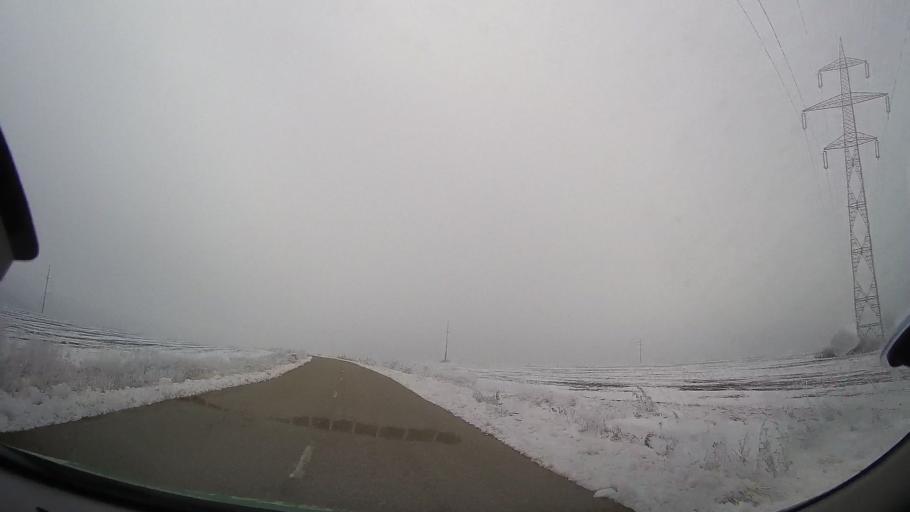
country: RO
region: Vaslui
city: Coroiesti
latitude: 46.2378
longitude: 27.4781
